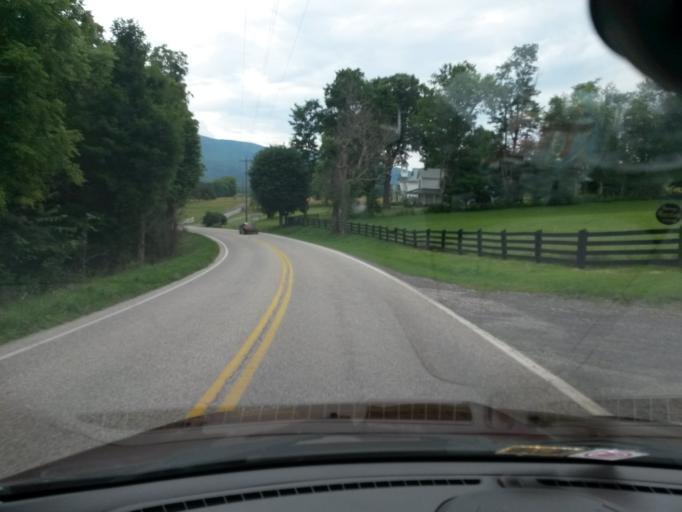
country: US
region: Virginia
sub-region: Alleghany County
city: Clifton Forge
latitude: 37.8915
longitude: -79.9081
